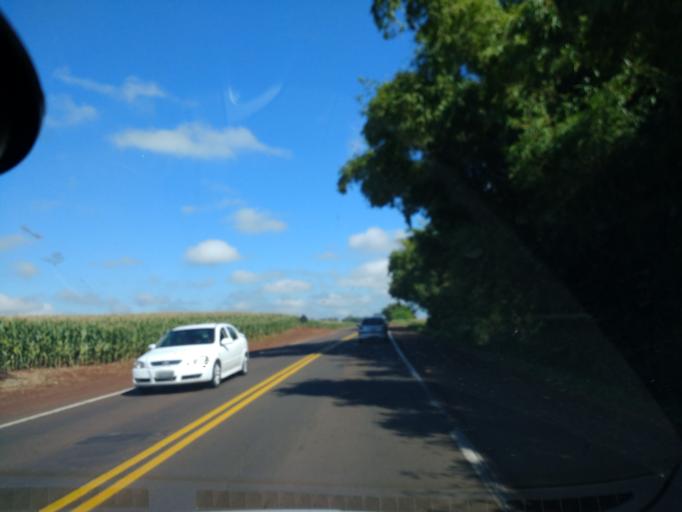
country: BR
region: Parana
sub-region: Paicandu
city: Paicandu
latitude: -23.5190
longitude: -52.1880
